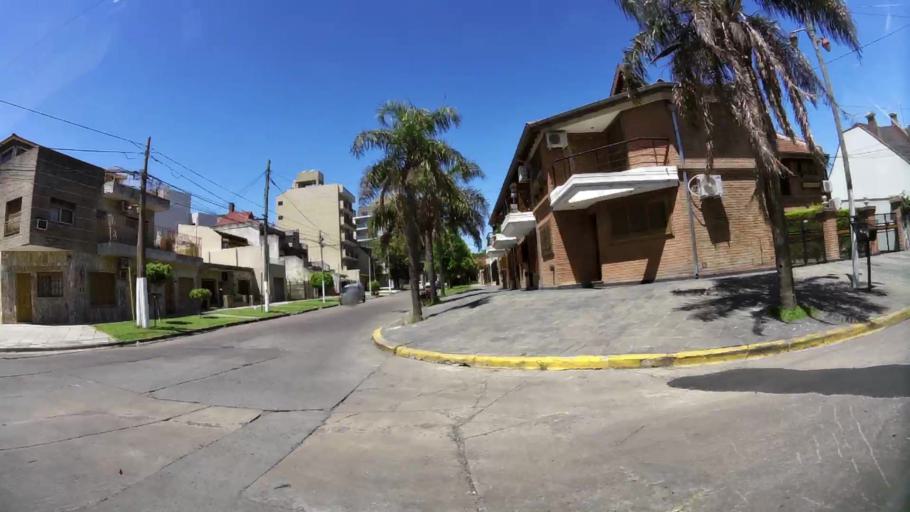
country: AR
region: Buenos Aires
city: Caseros
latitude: -34.5865
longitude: -58.5717
